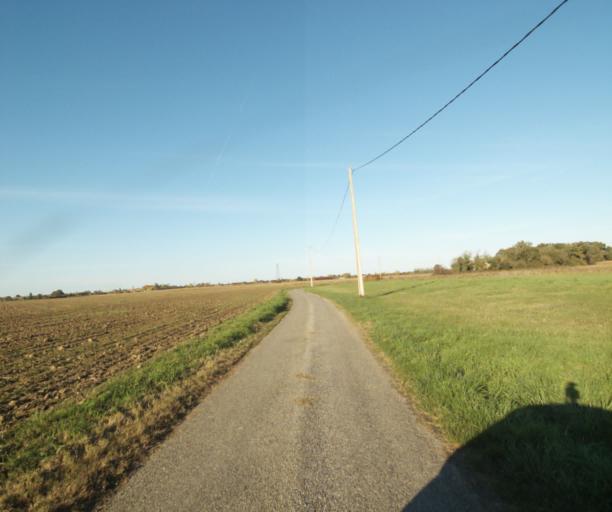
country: FR
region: Midi-Pyrenees
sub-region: Departement du Tarn-et-Garonne
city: Saint-Porquier
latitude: 43.9709
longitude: 1.1919
